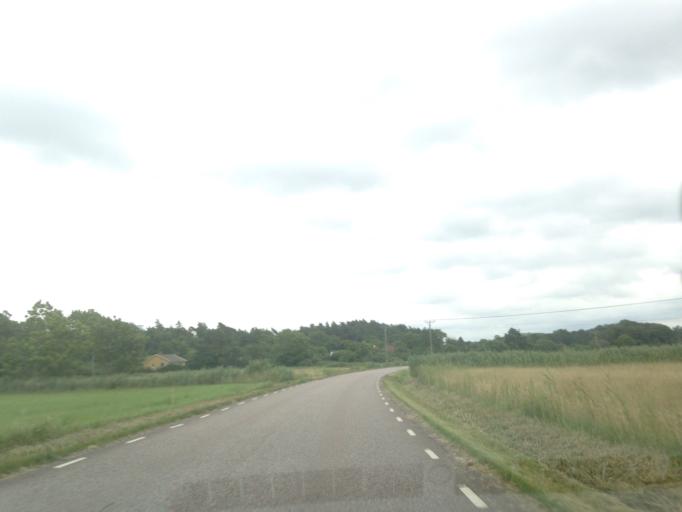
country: SE
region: Vaestra Goetaland
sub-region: Kungalvs Kommun
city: Kode
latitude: 57.8204
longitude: 11.8622
